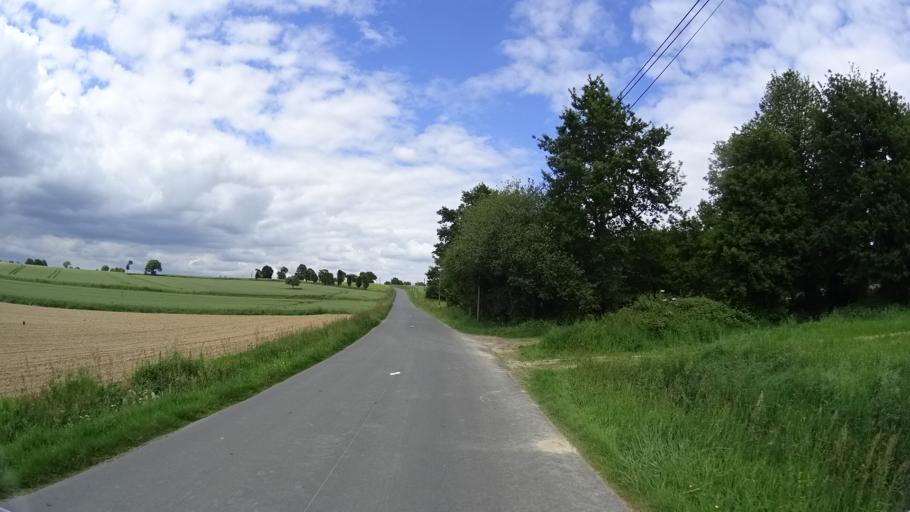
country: FR
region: Brittany
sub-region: Departement d'Ille-et-Vilaine
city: Iffendic
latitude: 48.0828
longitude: -2.1004
